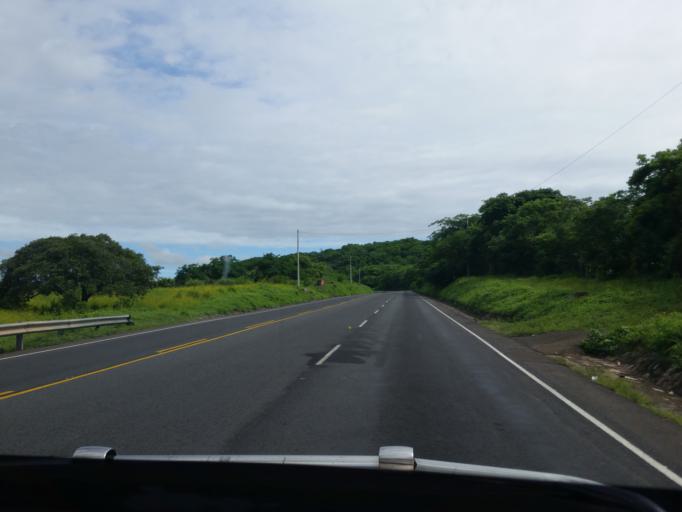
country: NI
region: Matagalpa
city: Ciudad Dario
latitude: 12.5158
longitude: -86.0535
